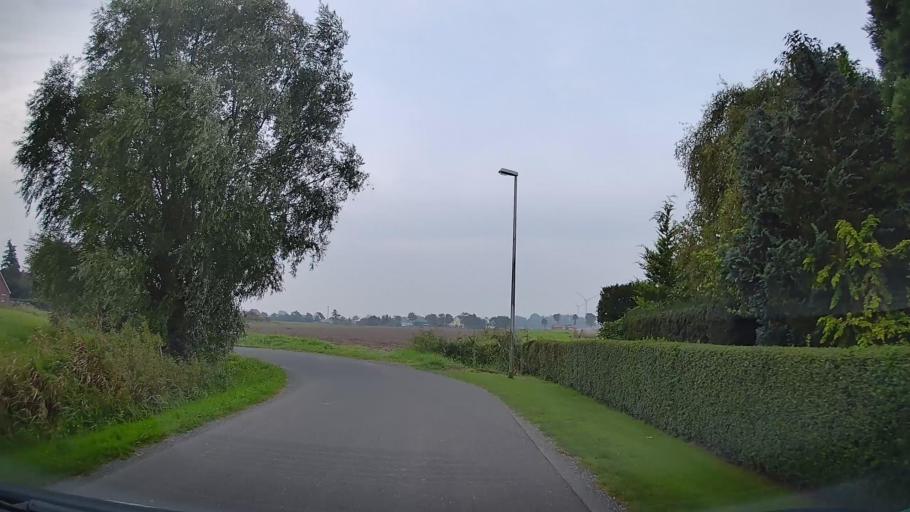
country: DE
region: Lower Saxony
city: Cuxhaven
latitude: 53.8315
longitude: 8.7602
